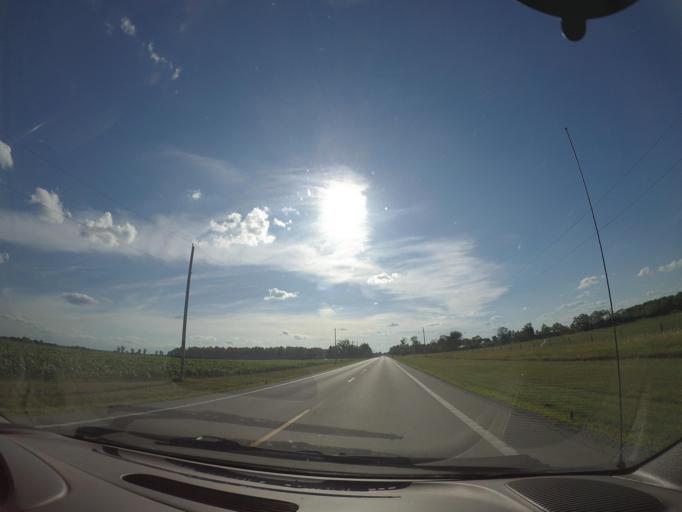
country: US
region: Ohio
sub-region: Henry County
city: Napoleon
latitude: 41.4308
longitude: -84.2135
